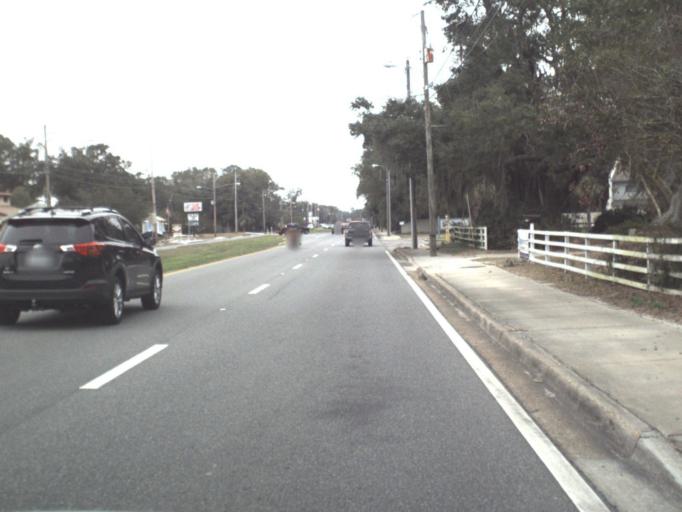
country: US
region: Florida
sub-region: Bay County
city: Parker
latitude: 30.1144
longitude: -85.5993
